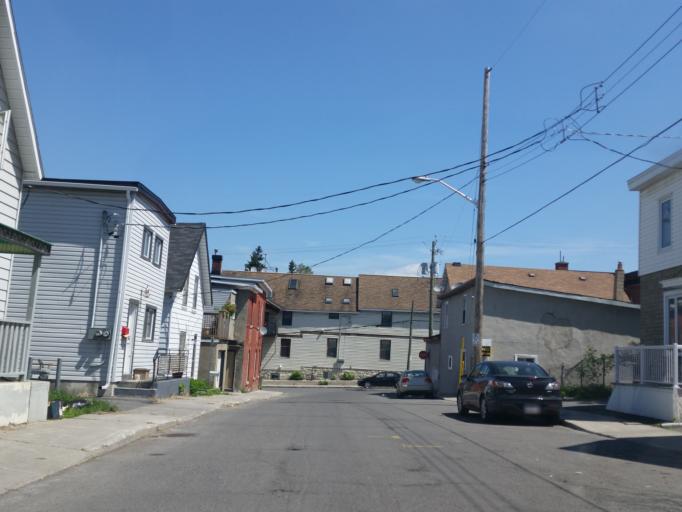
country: CA
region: Ontario
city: Ottawa
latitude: 45.4061
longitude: -75.7247
